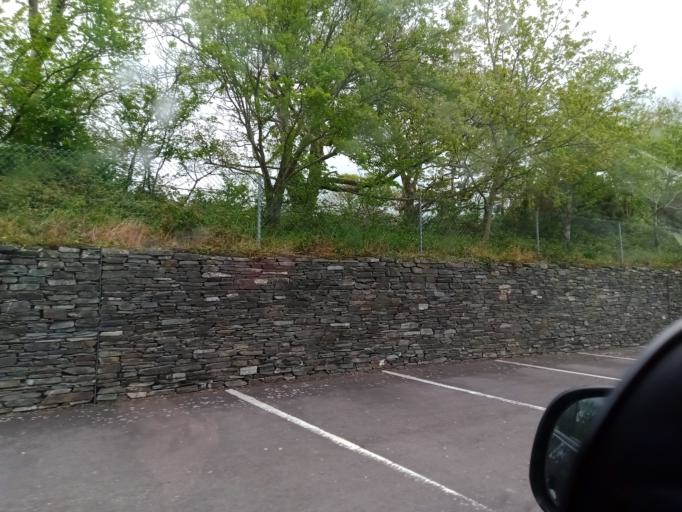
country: IE
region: Munster
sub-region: County Cork
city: Clonakilty
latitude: 51.6217
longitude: -8.9047
